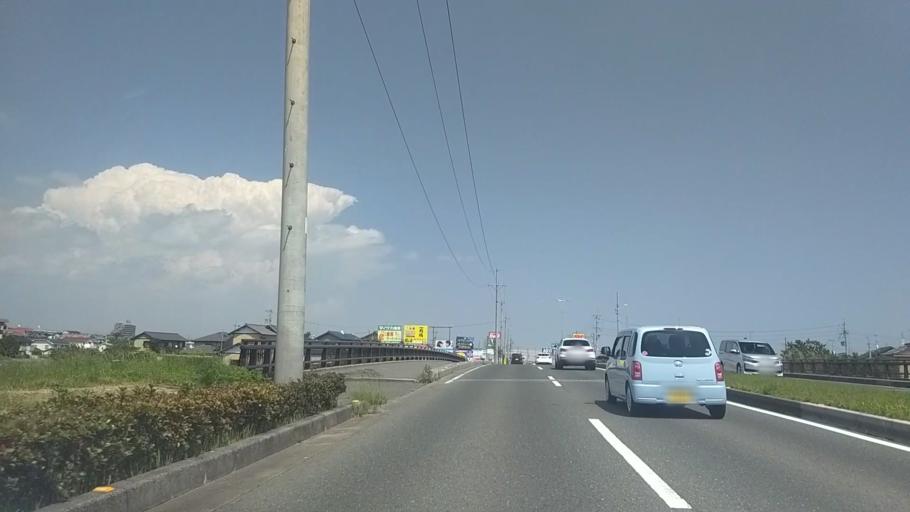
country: JP
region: Shizuoka
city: Hamamatsu
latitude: 34.6988
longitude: 137.6670
